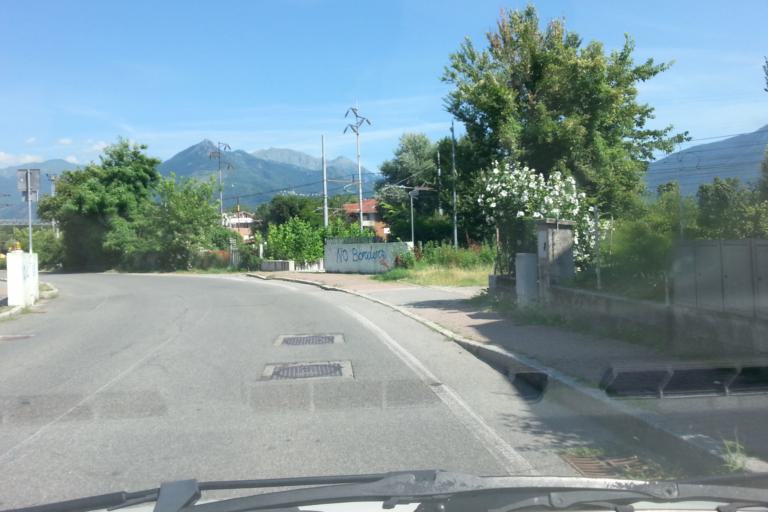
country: IT
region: Piedmont
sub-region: Provincia di Torino
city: Avigliana
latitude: 45.0866
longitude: 7.3953
